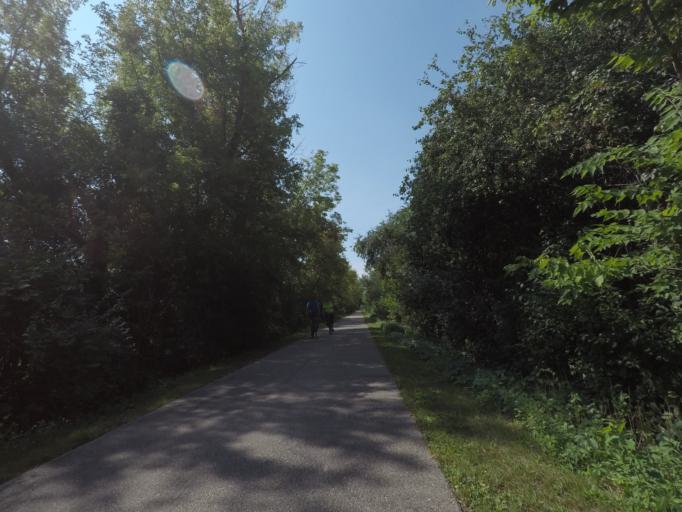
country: US
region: Wisconsin
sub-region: Jefferson County
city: Fort Atkinson
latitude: 42.9028
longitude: -88.8594
